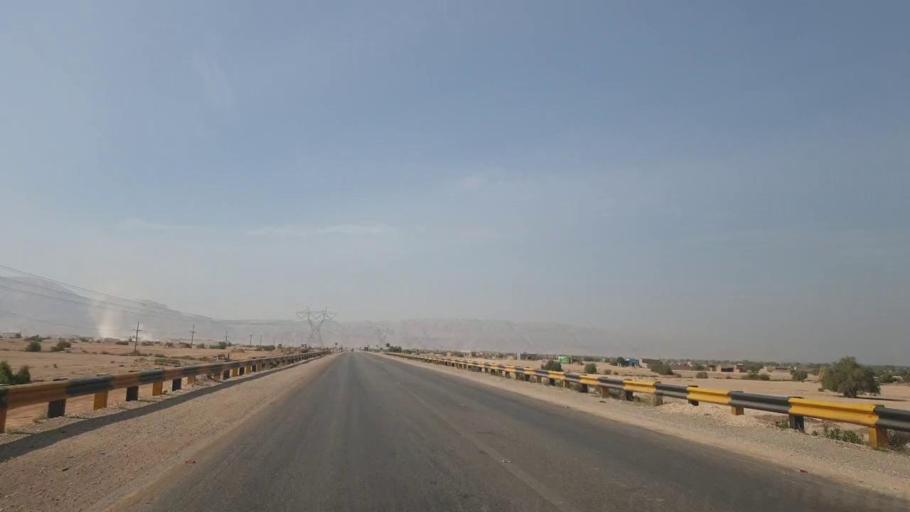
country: PK
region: Sindh
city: Sehwan
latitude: 26.2065
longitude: 67.9295
